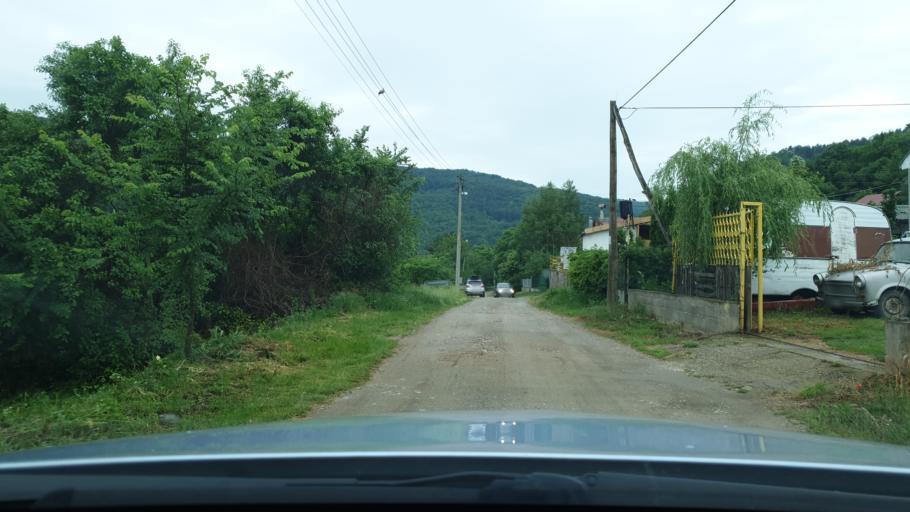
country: RS
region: Central Serbia
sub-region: Zajecarski Okrug
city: Soko Banja
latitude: 43.6597
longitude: 21.7630
